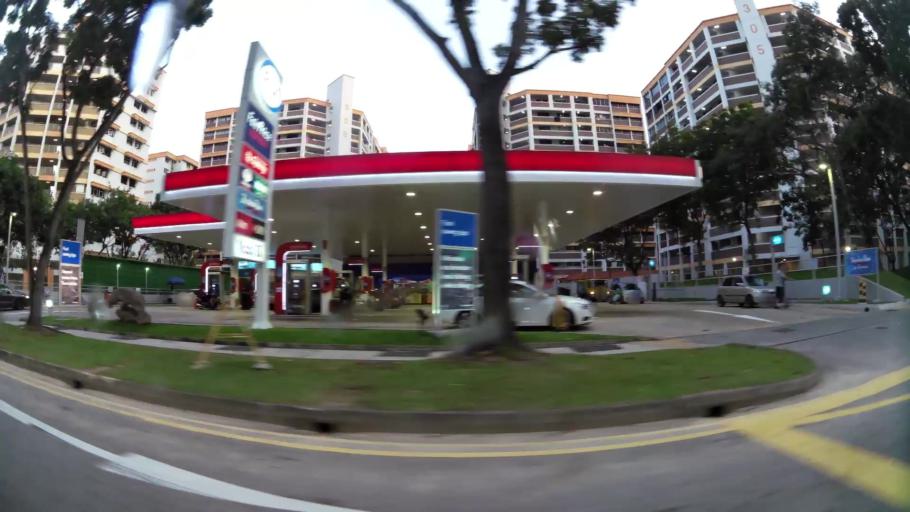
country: MY
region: Johor
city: Kampung Pasir Gudang Baru
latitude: 1.4318
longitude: 103.8396
